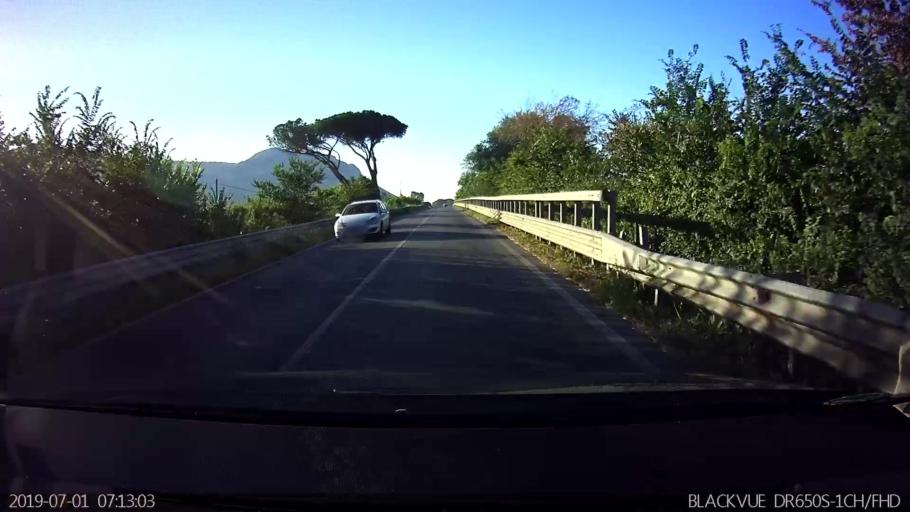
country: IT
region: Latium
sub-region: Provincia di Latina
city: Borgo Hermada
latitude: 41.3302
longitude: 13.1729
